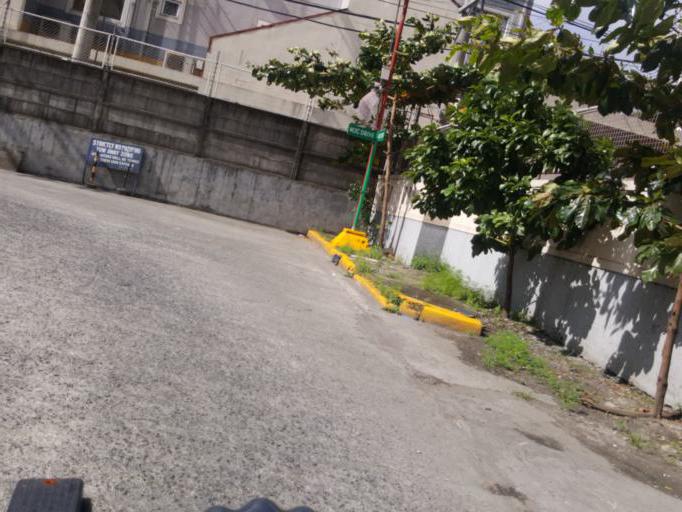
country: PH
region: Metro Manila
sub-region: City of Manila
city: Manila
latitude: 14.6190
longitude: 120.9870
